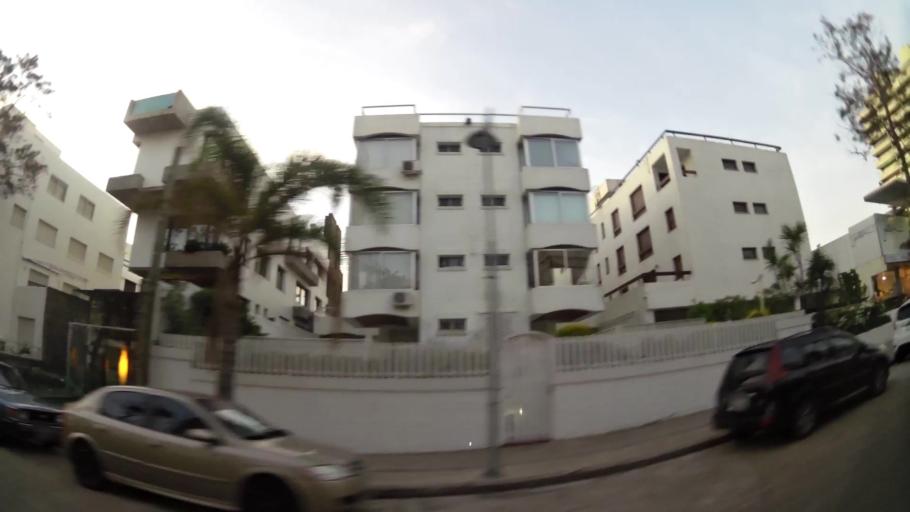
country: UY
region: Maldonado
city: Punta del Este
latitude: -34.9620
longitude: -54.9452
